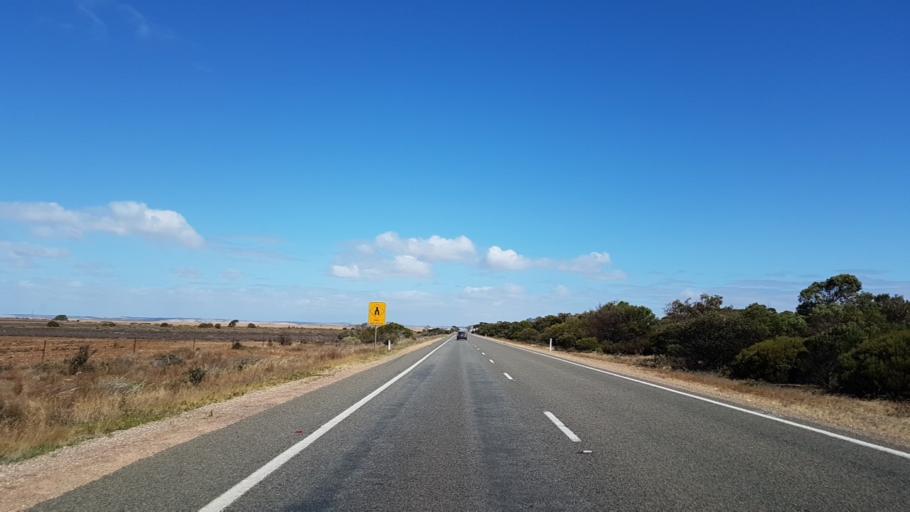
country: AU
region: South Australia
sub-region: Wakefield
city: Balaklava
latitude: -34.2116
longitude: 138.1828
